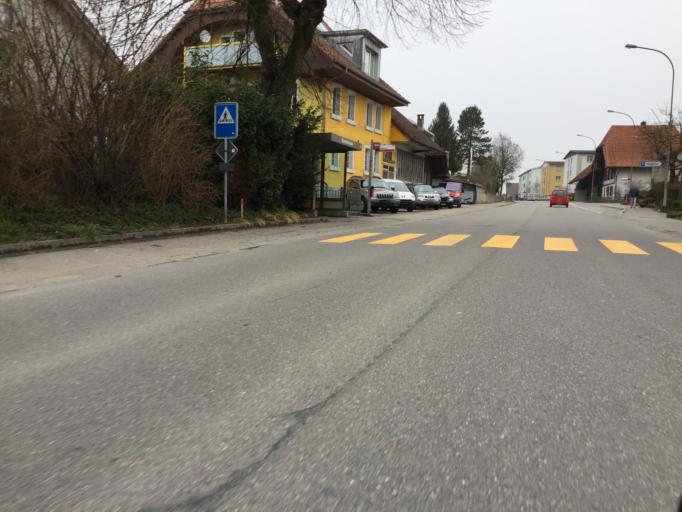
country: CH
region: Bern
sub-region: Biel/Bienne District
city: Orpund
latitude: 47.1392
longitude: 7.3121
